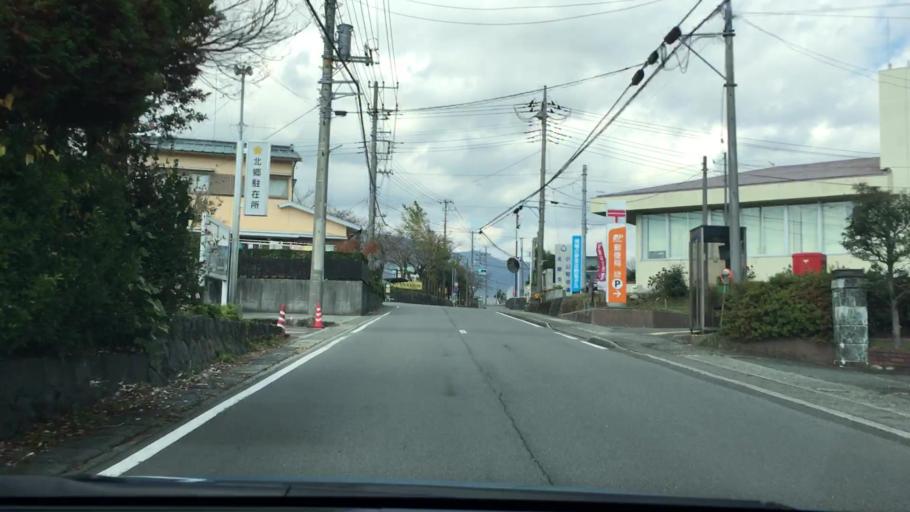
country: JP
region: Shizuoka
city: Gotemba
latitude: 35.3436
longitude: 138.9441
